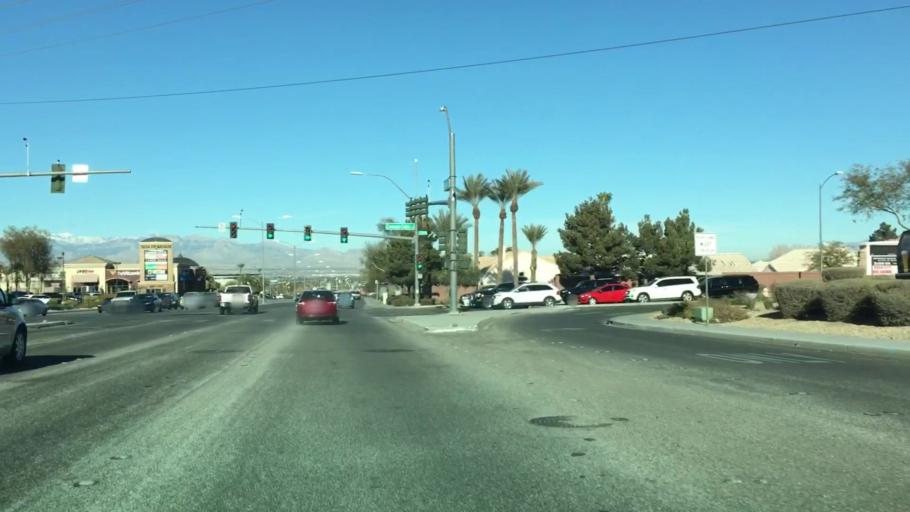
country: US
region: Nevada
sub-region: Clark County
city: Whitney
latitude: 36.0023
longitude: -115.1084
